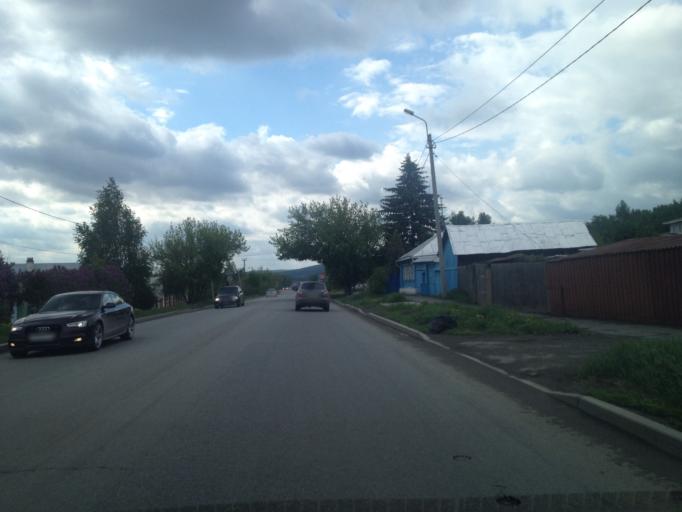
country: RU
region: Sverdlovsk
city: Istok
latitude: 56.7418
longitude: 60.7004
